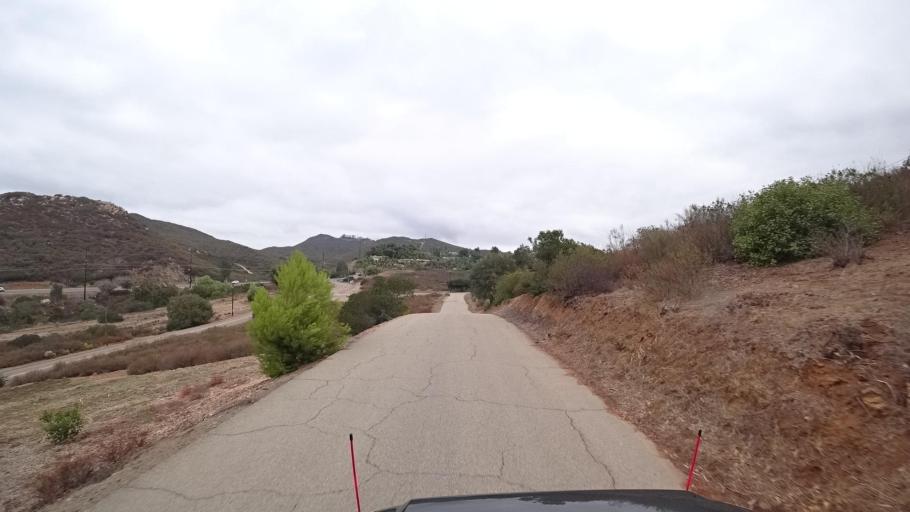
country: US
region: California
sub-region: San Diego County
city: Escondido
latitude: 33.0814
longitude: -117.1178
